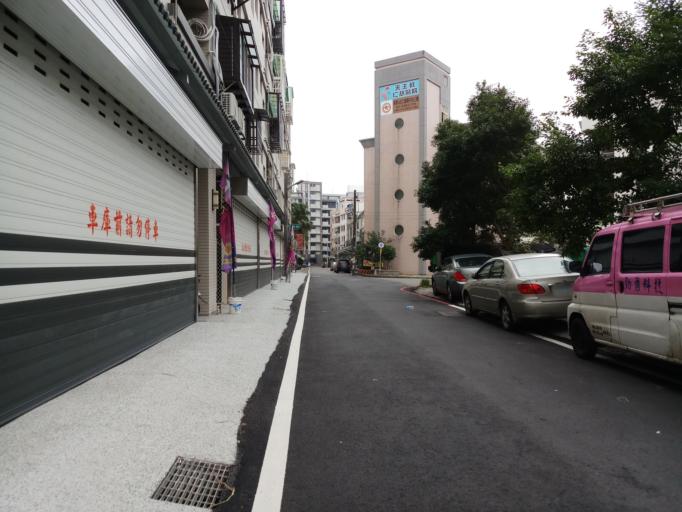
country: TW
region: Taiwan
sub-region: Hsinchu
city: Zhubei
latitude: 24.8665
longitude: 121.0267
